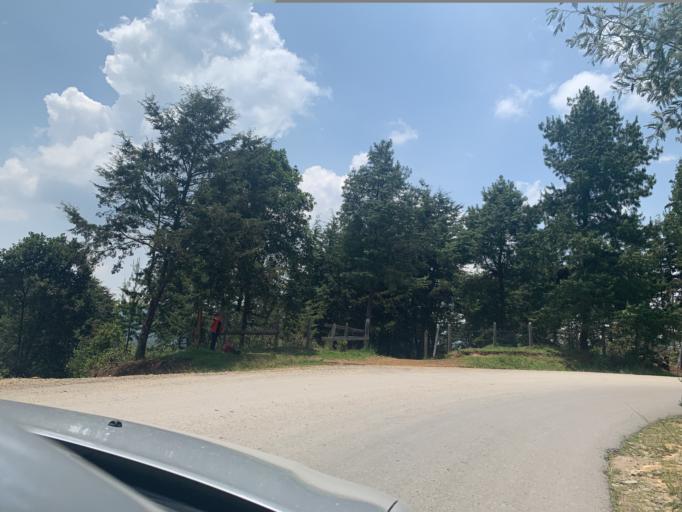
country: CO
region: Boyaca
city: Chiquinquira
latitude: 5.5788
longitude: -73.7490
